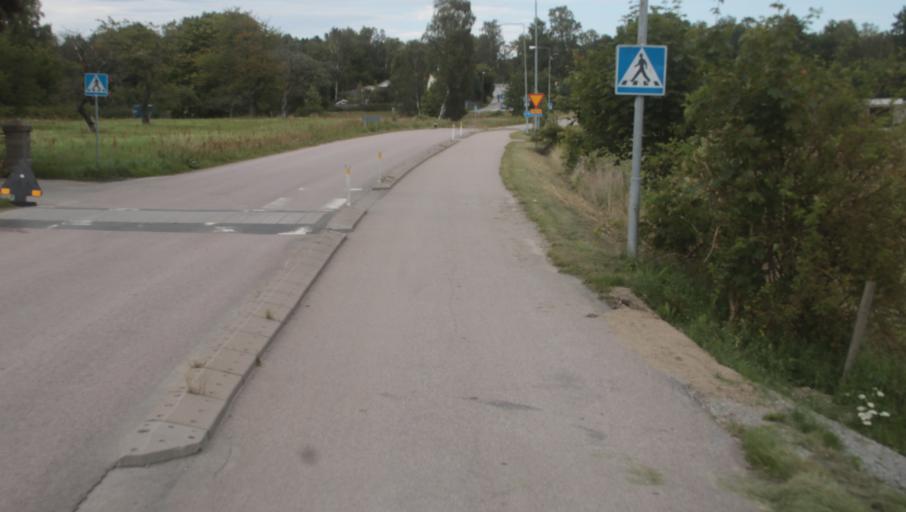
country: SE
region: Blekinge
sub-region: Karlshamns Kommun
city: Karlshamn
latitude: 56.2160
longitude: 14.8463
